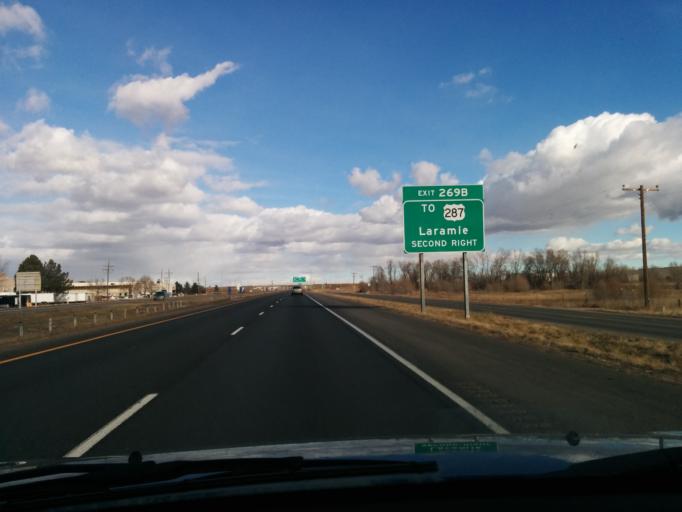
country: US
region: Colorado
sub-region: Larimer County
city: Fort Collins
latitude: 40.5745
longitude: -105.0012
